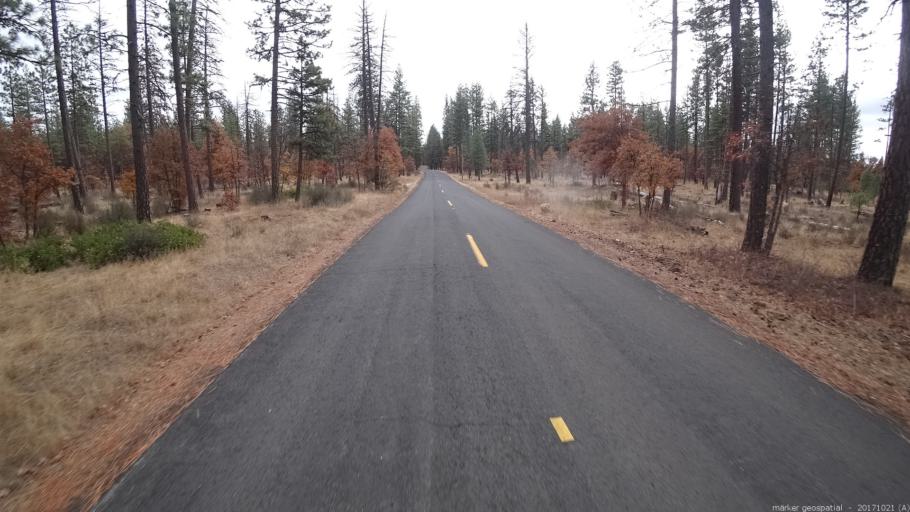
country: US
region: California
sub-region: Shasta County
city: Burney
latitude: 40.9391
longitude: -121.6444
